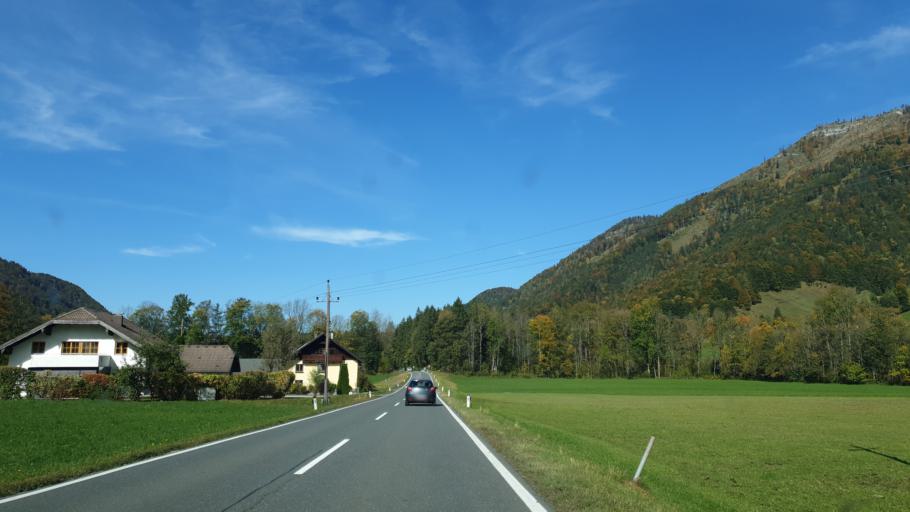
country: AT
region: Salzburg
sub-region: Politischer Bezirk Salzburg-Umgebung
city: Hintersee
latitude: 47.7329
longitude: 13.2659
